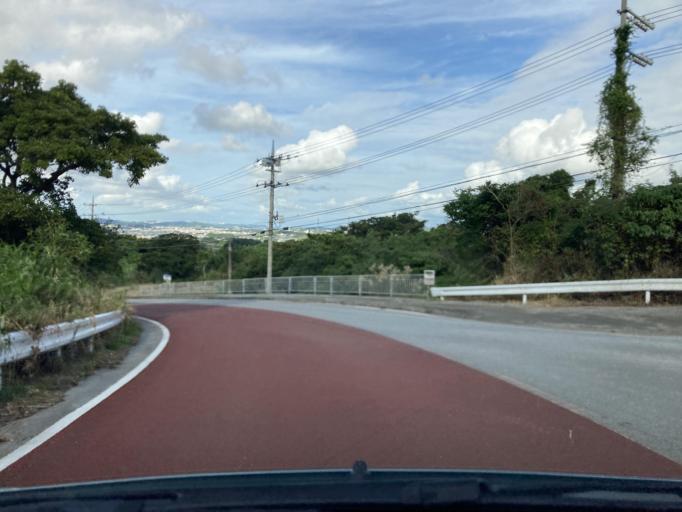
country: JP
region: Okinawa
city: Itoman
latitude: 26.1284
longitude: 127.7128
